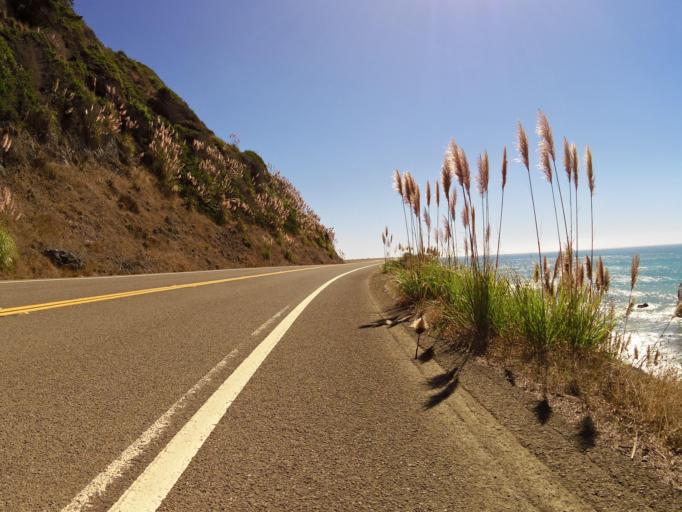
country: US
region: California
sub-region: Mendocino County
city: Fort Bragg
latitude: 39.7084
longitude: -123.8061
